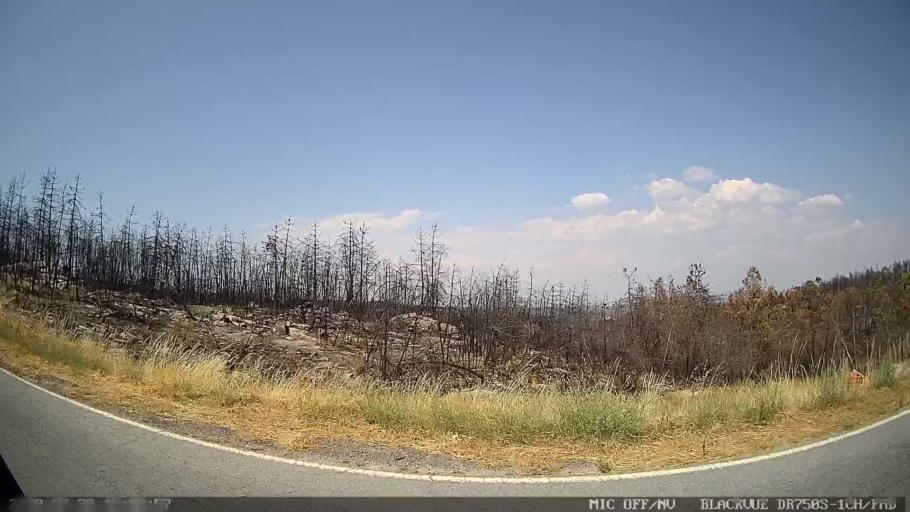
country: PT
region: Vila Real
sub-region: Murca
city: Murca
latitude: 41.3692
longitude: -7.4971
